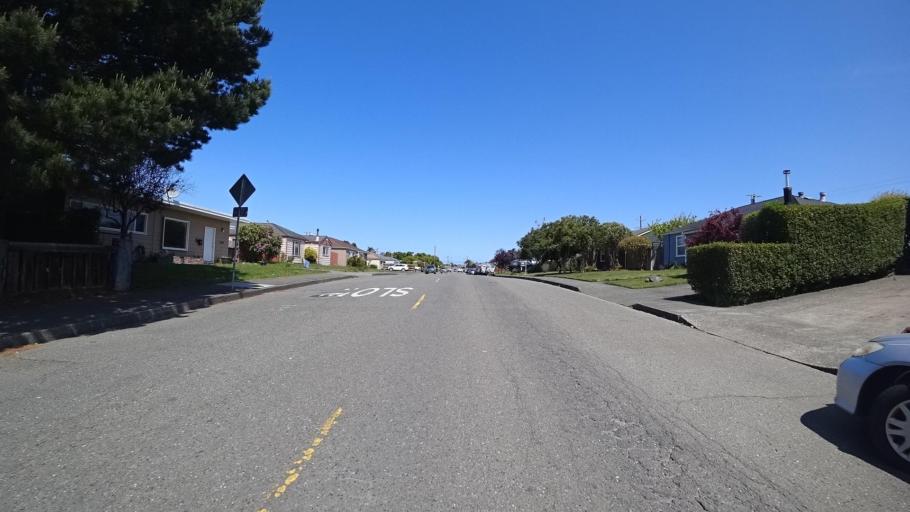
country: US
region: California
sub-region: Humboldt County
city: Bayview
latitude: 40.7771
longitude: -124.1834
